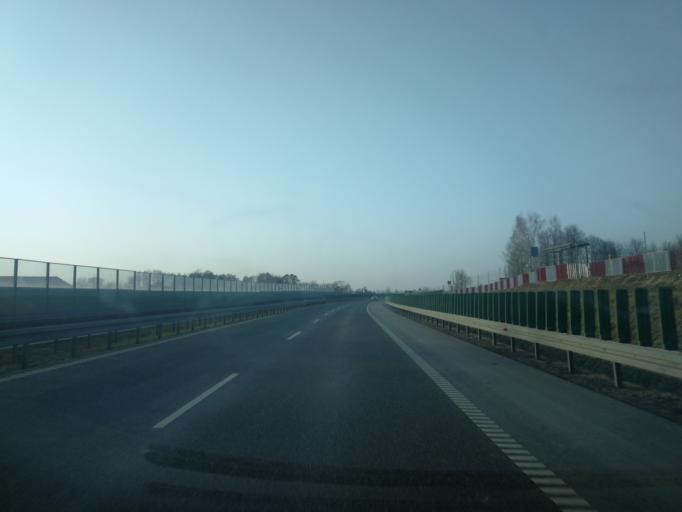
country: PL
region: Warmian-Masurian Voivodeship
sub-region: Powiat elblaski
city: Gronowo Gorne
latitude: 54.1227
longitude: 19.4656
